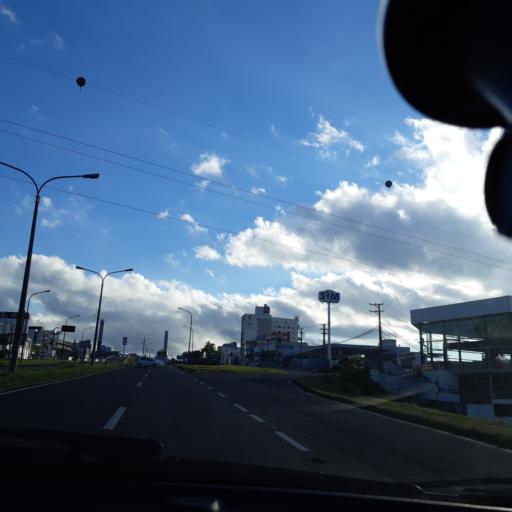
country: BR
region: Rio Grande do Sul
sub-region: Caxias Do Sul
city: Caxias do Sul
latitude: -29.1752
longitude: -51.2121
